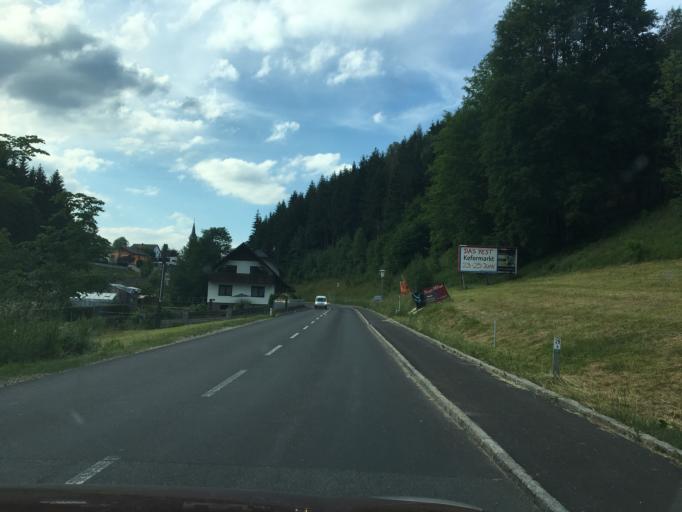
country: AT
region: Upper Austria
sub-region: Politischer Bezirk Urfahr-Umgebung
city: Reichenau im Muhlkreis
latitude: 48.4510
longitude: 14.3535
